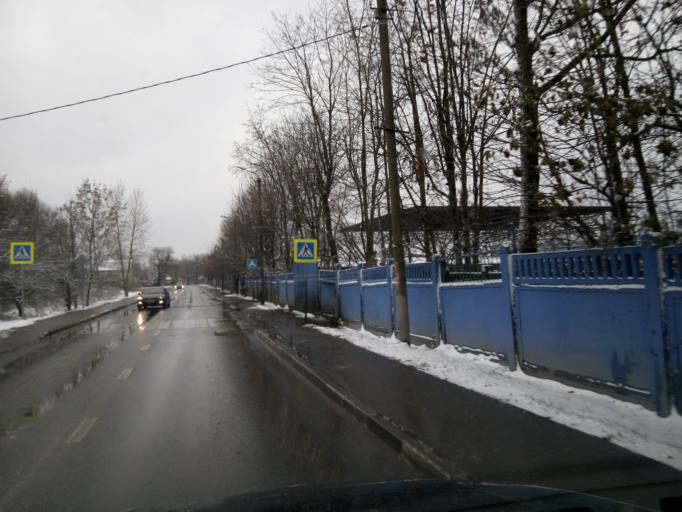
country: RU
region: Moskovskaya
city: Skhodnya
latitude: 55.9424
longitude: 37.2789
